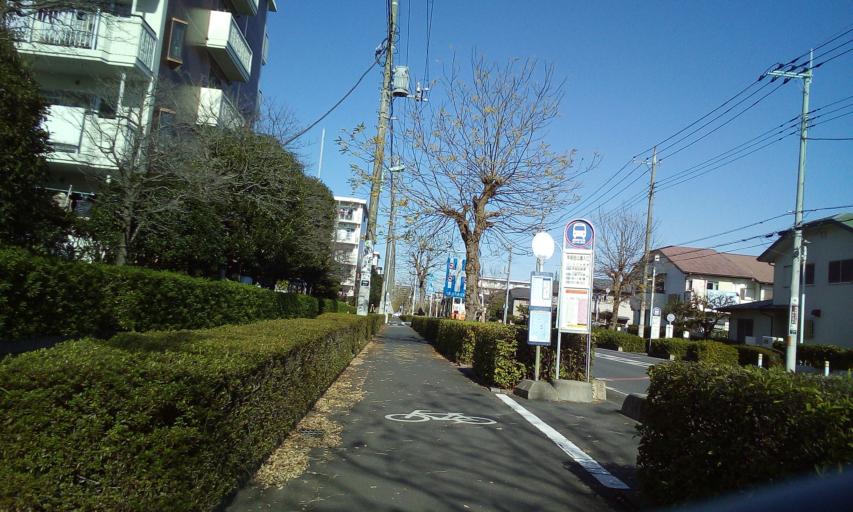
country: JP
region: Chiba
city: Nagareyama
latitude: 35.8507
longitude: 139.8852
